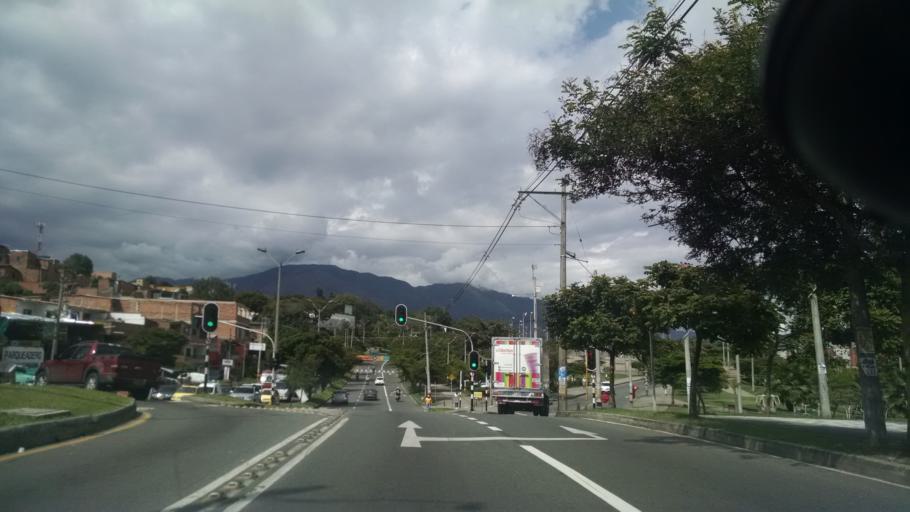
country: CO
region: Antioquia
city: Medellin
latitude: 6.2913
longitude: -75.5695
